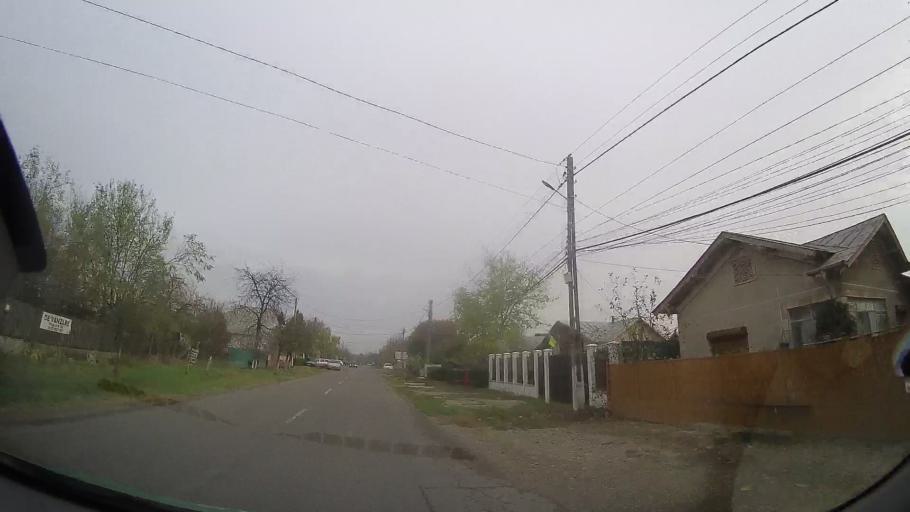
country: RO
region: Prahova
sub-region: Comuna Balta Doamnei
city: Balta Doamnei
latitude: 44.7630
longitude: 26.1527
